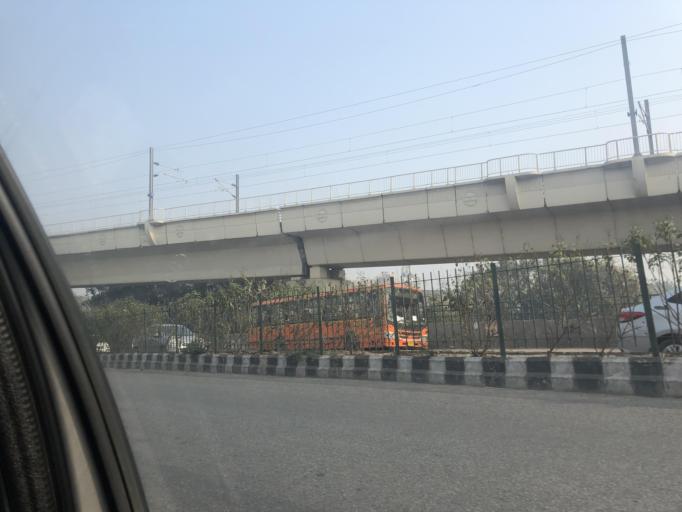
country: IN
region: NCT
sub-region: North West Delhi
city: Pitampura
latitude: 28.6322
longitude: 77.1320
